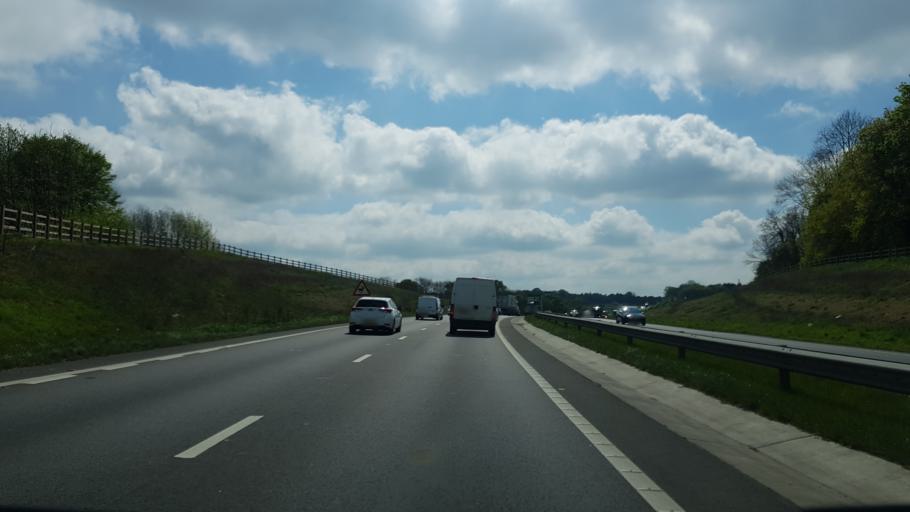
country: GB
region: England
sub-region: Kent
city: Tonbridge
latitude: 51.1734
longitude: 0.3006
